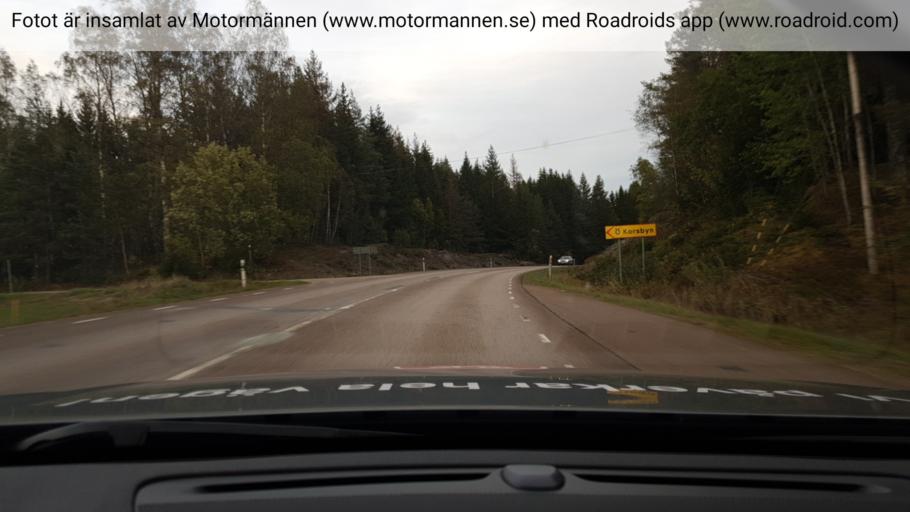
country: SE
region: Vaestra Goetaland
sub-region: Amals Kommun
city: Amal
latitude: 59.0714
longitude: 12.6488
